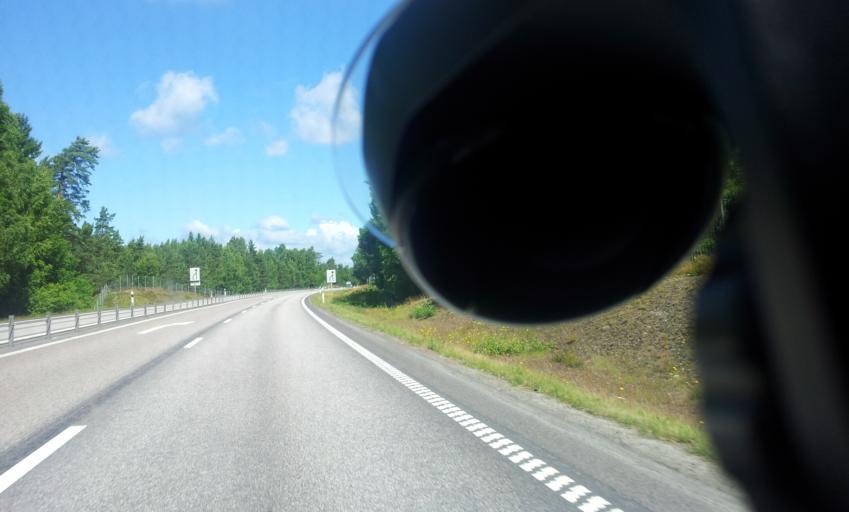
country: SE
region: Kalmar
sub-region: Oskarshamns Kommun
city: Paskallavik
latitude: 57.1606
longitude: 16.4477
